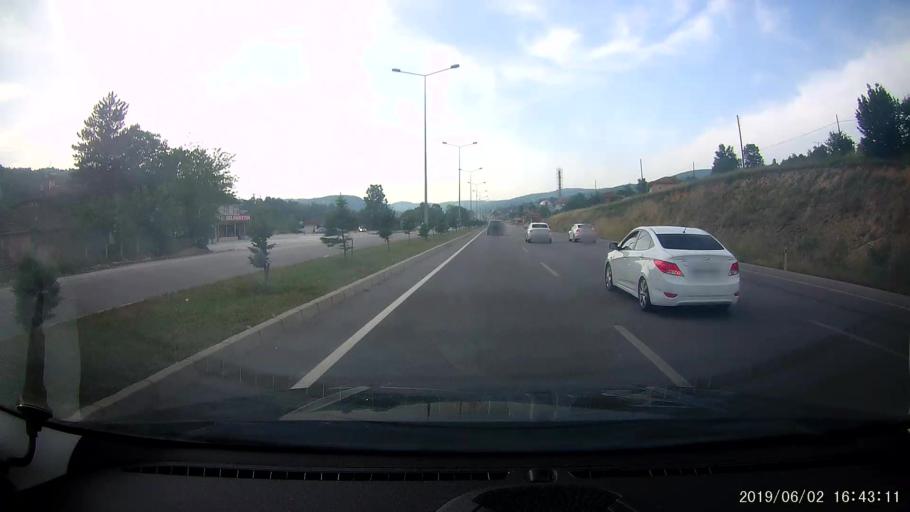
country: TR
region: Samsun
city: Kavak
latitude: 41.1311
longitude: 36.1324
